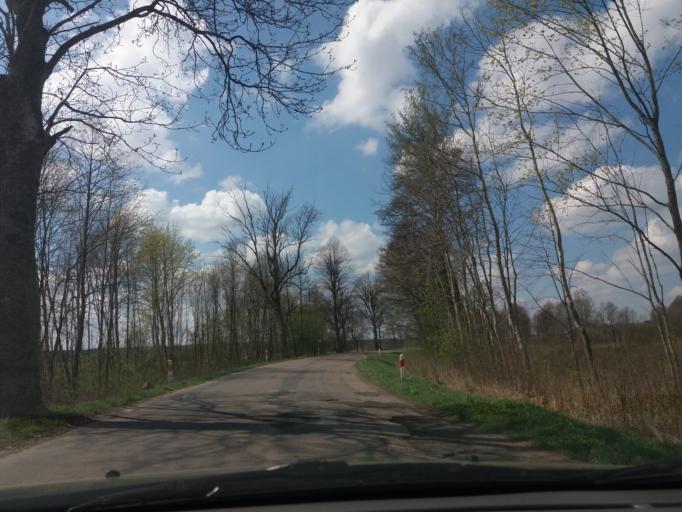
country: PL
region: Warmian-Masurian Voivodeship
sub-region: Powiat szczycienski
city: Jedwabno
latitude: 53.3571
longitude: 20.6741
